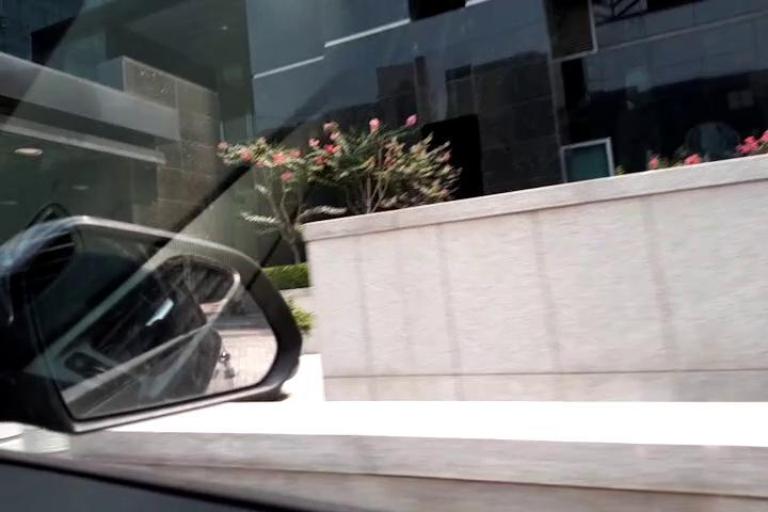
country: KR
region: Seoul
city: Seoul
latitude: 37.5003
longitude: 127.0339
